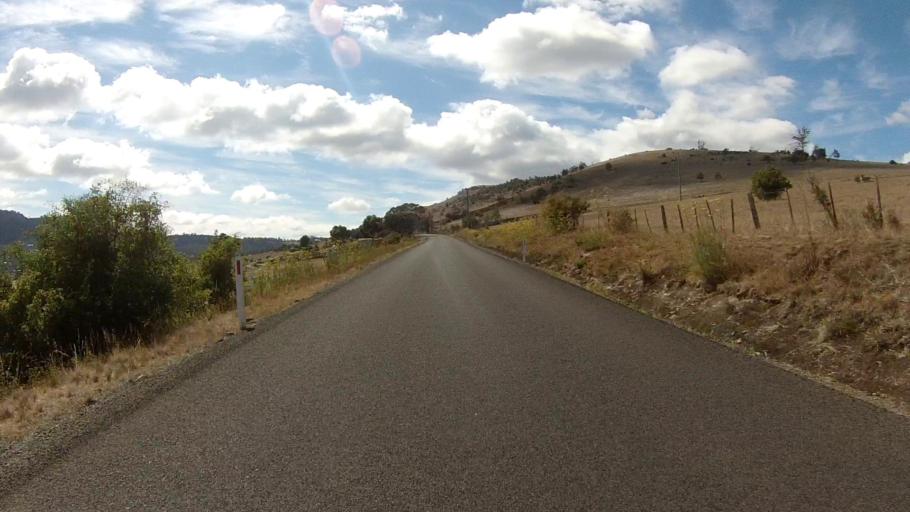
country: AU
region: Tasmania
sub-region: Brighton
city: Bridgewater
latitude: -42.7284
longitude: 147.2669
